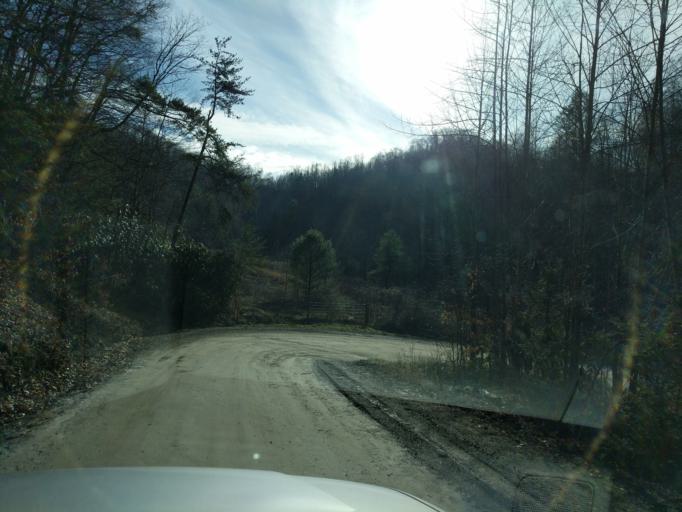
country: US
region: North Carolina
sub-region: Haywood County
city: Cove Creek
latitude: 35.6694
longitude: -83.0292
